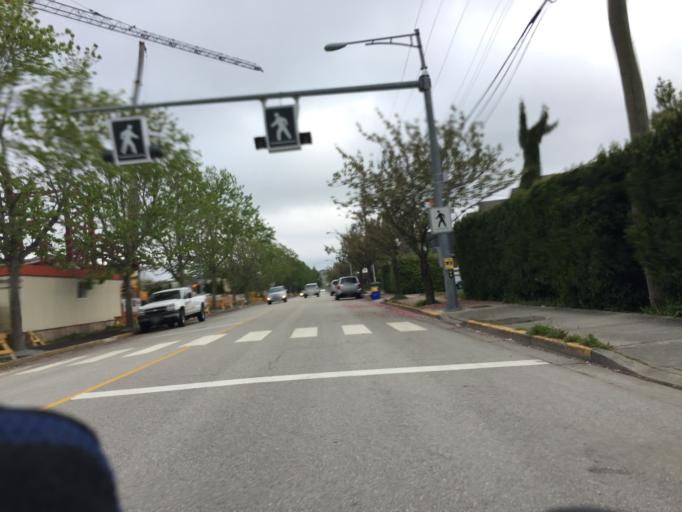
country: CA
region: British Columbia
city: Richmond
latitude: 49.1527
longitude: -123.1309
